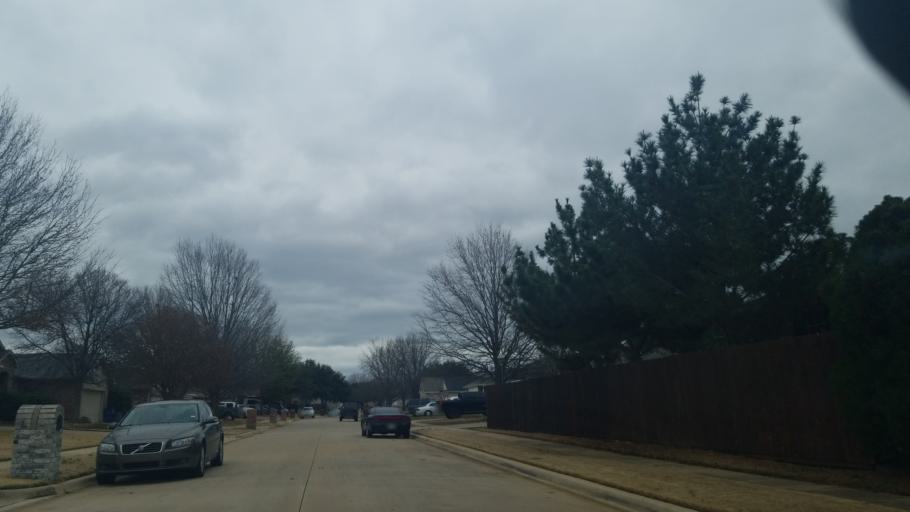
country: US
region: Texas
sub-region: Denton County
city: Corinth
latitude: 33.1354
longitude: -97.0888
